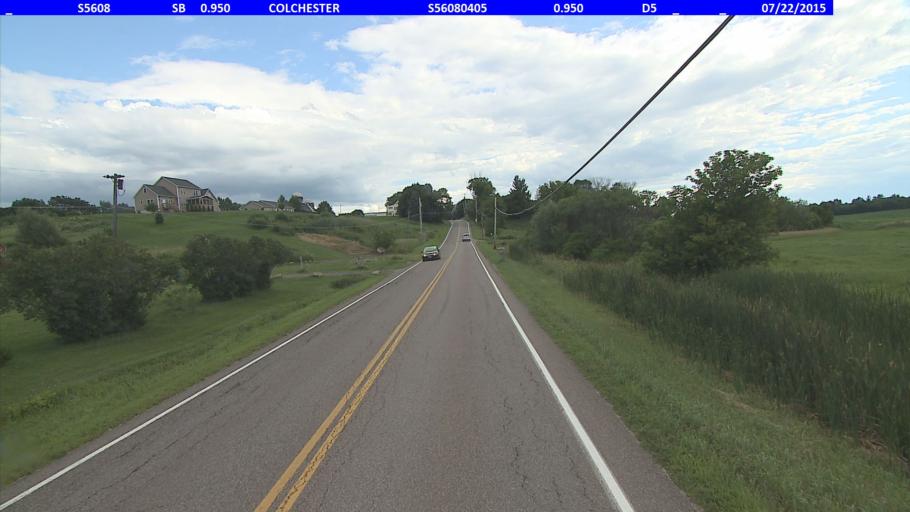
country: US
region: Vermont
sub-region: Chittenden County
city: Winooski
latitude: 44.5126
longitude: -73.2028
